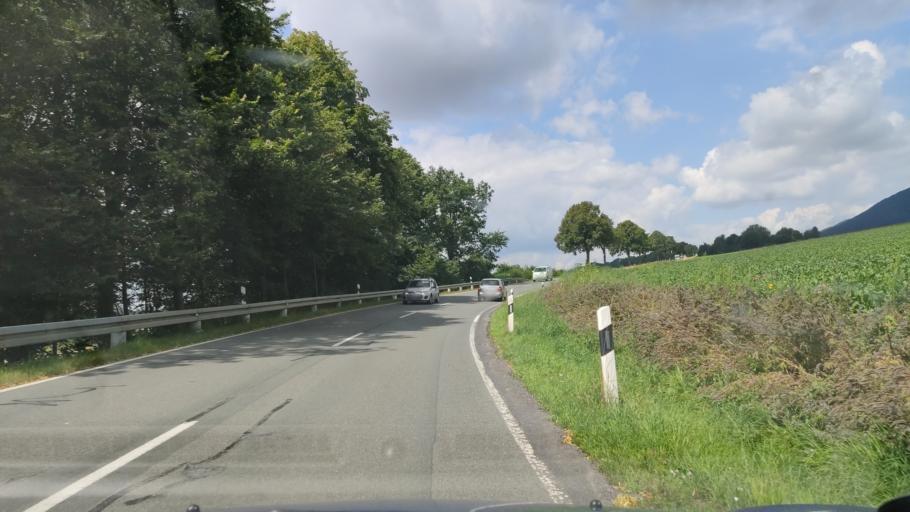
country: DE
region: Lower Saxony
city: Heyen
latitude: 52.0493
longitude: 9.5369
